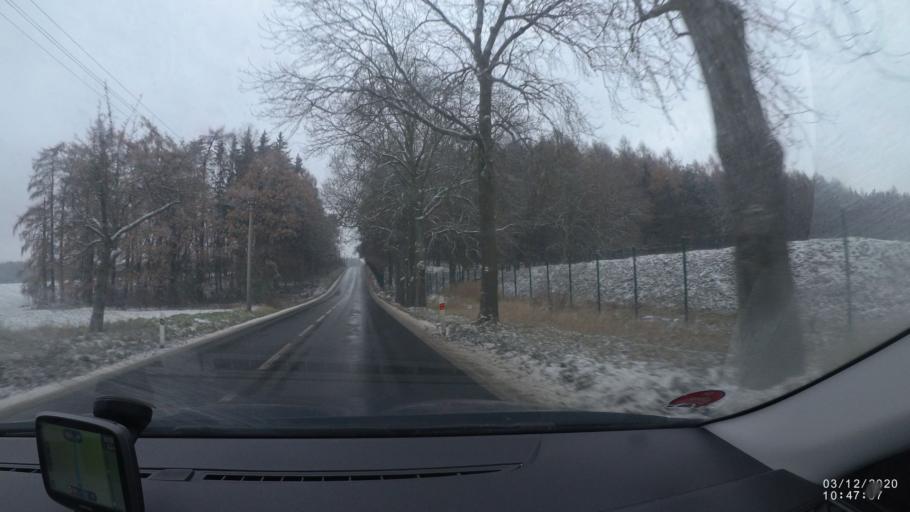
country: CZ
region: Central Bohemia
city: Nove Straseci
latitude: 50.1670
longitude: 13.8987
